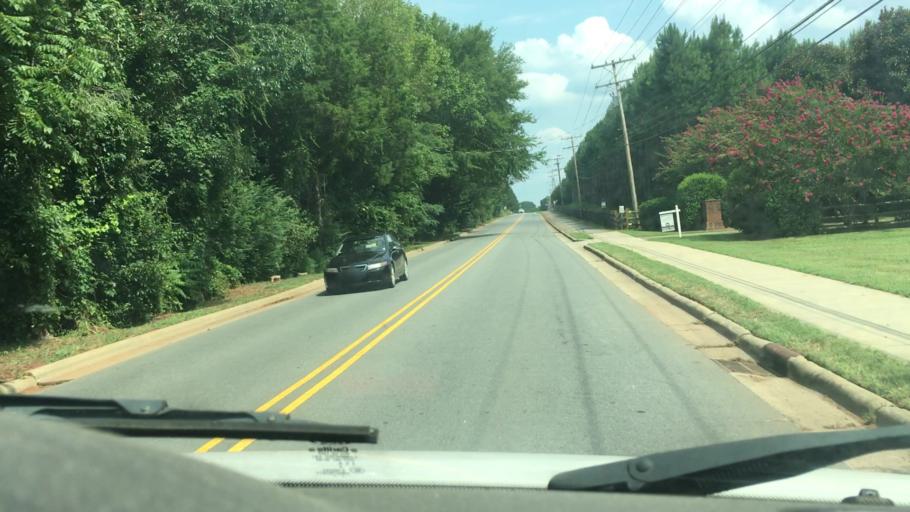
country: US
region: North Carolina
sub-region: Gaston County
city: Davidson
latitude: 35.4879
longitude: -80.8261
